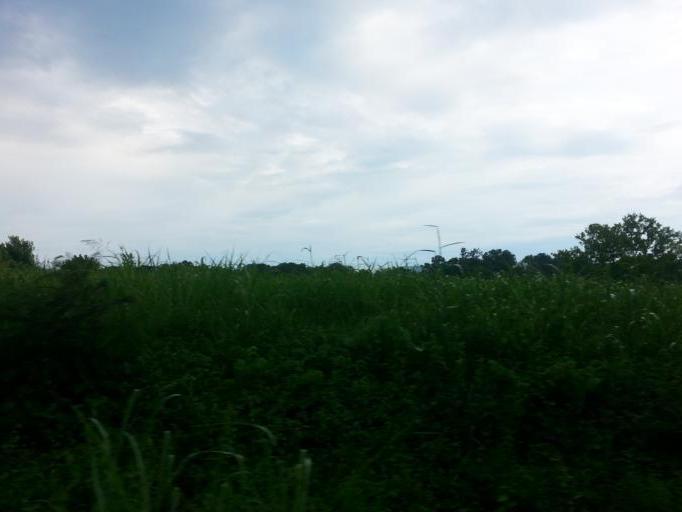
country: US
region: Tennessee
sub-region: Sevier County
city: Seymour
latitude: 35.8539
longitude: -83.7540
